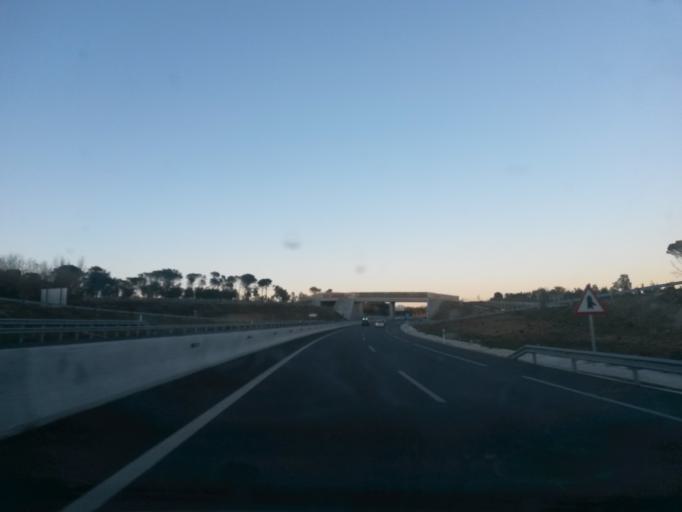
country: ES
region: Catalonia
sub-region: Provincia de Girona
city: Sils
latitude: 41.8348
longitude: 2.7588
